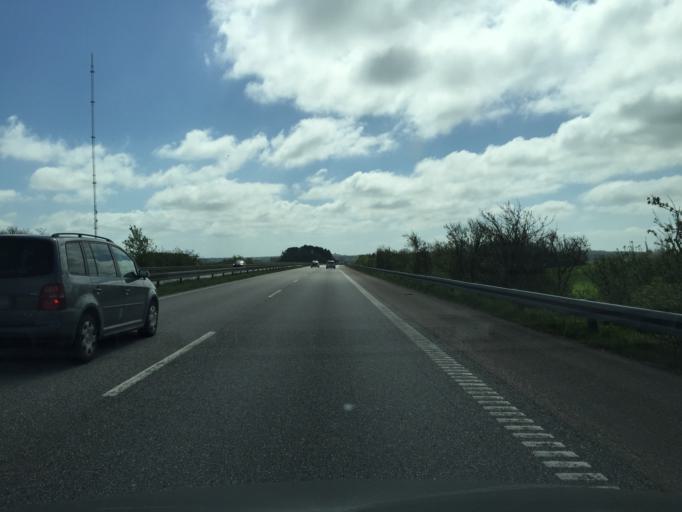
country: DK
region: Zealand
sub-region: Vordingborg Kommune
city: Orslev
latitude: 55.0567
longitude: 11.9754
